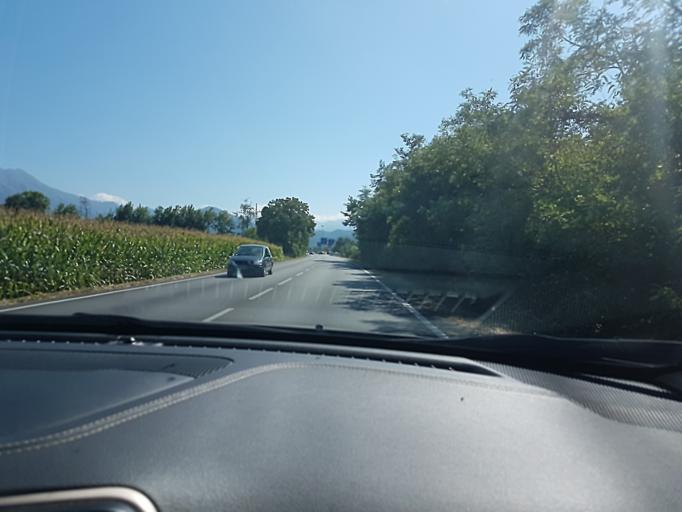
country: IT
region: Piedmont
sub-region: Provincia di Cuneo
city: Cuneo
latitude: 44.3738
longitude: 7.5540
